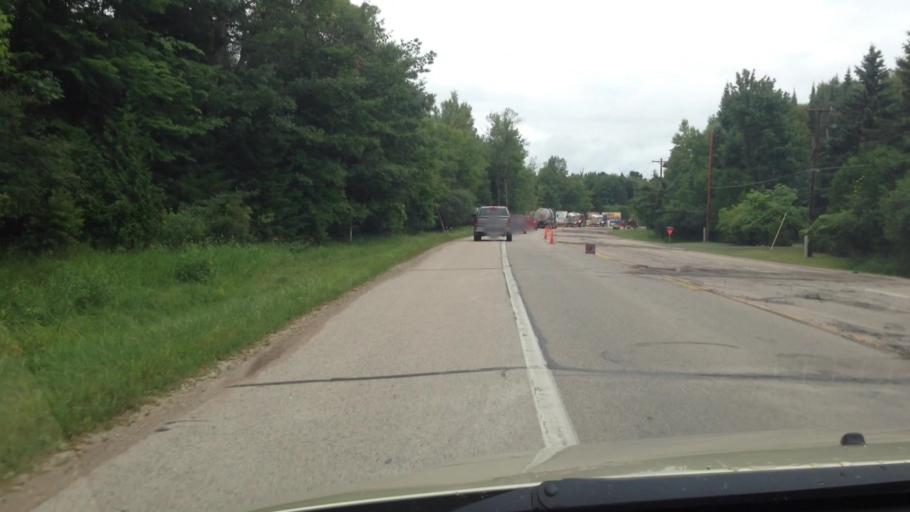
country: US
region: Michigan
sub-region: Delta County
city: Escanaba
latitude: 45.7030
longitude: -87.1011
